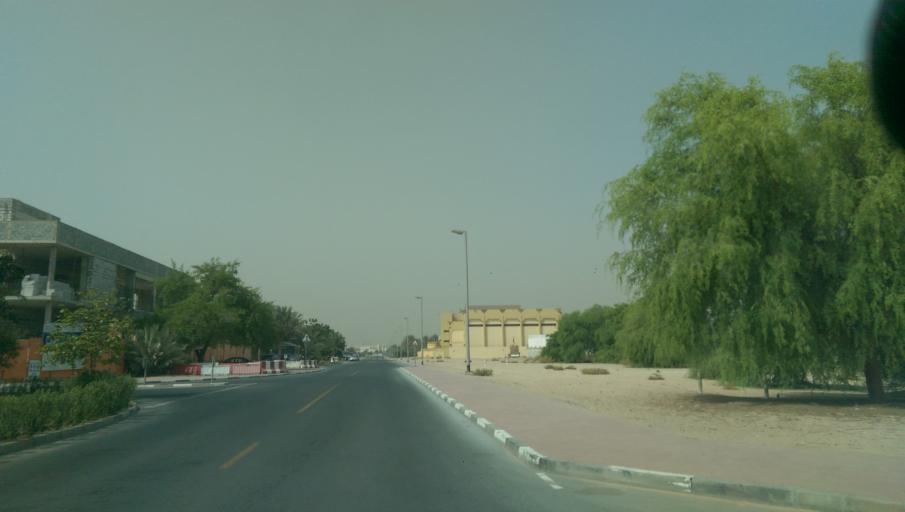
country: AE
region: Dubai
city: Dubai
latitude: 25.1555
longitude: 55.2244
